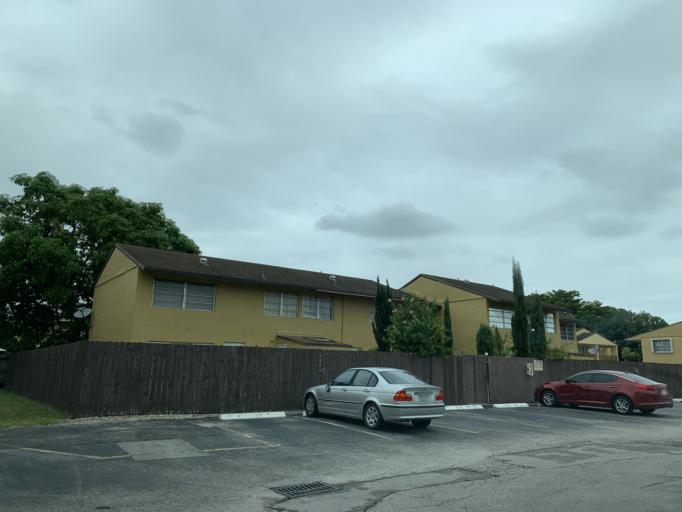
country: US
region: Florida
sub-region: Miami-Dade County
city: Kendall West
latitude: 25.6904
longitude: -80.4432
